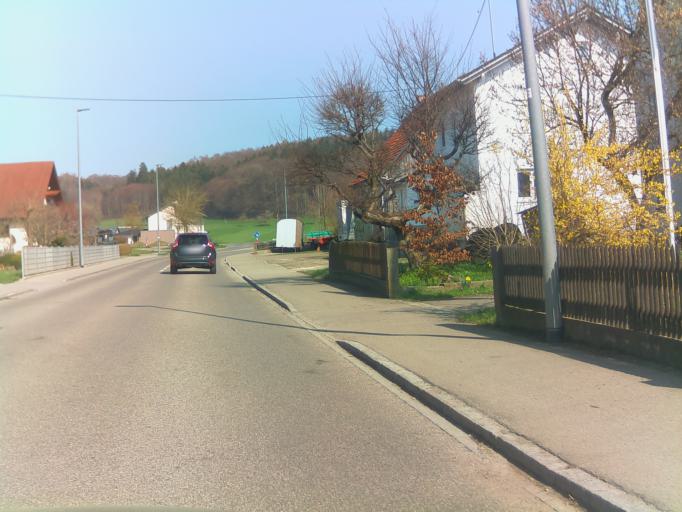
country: DE
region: Bavaria
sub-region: Swabia
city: Unterroth
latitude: 48.1971
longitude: 10.1734
